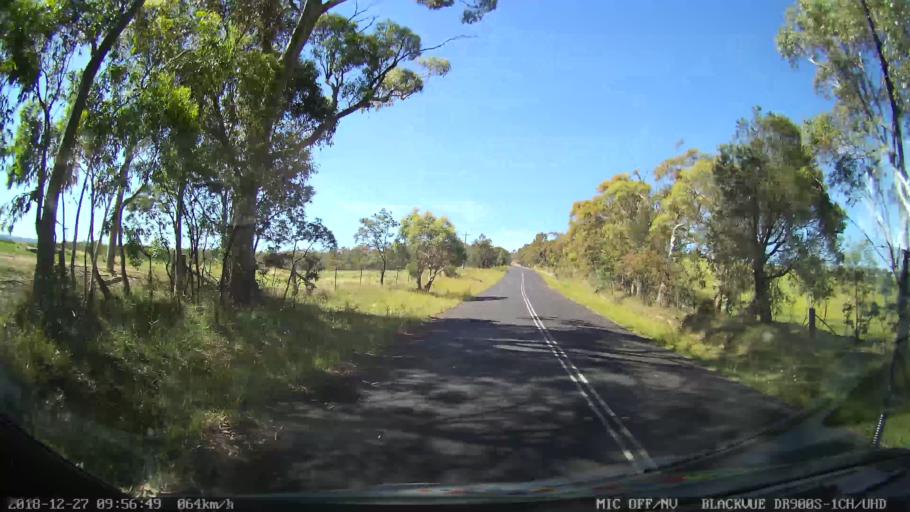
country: AU
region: New South Wales
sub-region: Lithgow
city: Portland
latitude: -33.4161
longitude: 149.9719
